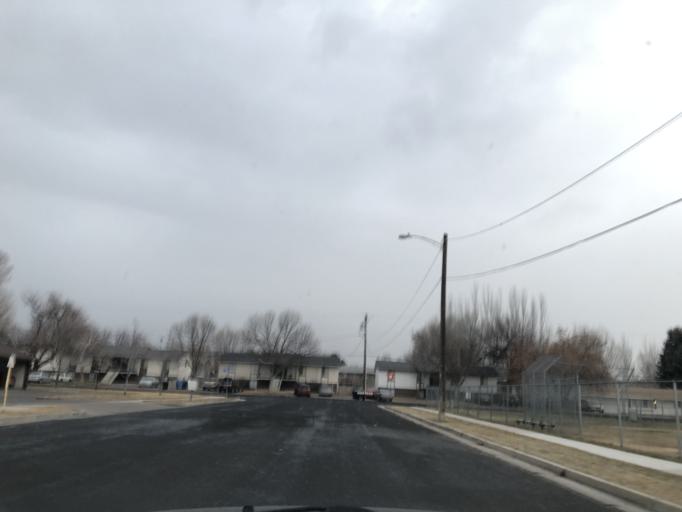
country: US
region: Utah
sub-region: Cache County
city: Logan
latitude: 41.7187
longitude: -111.8434
